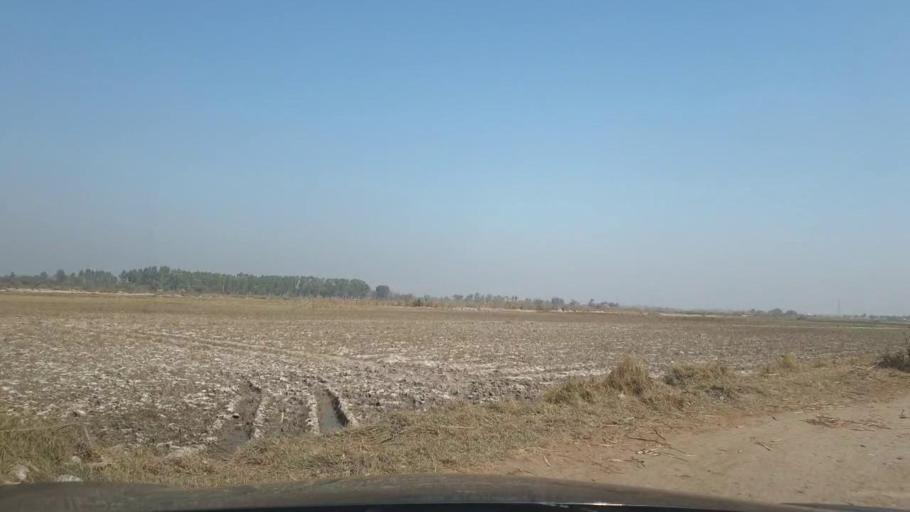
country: PK
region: Sindh
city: Ubauro
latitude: 28.1459
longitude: 69.6976
